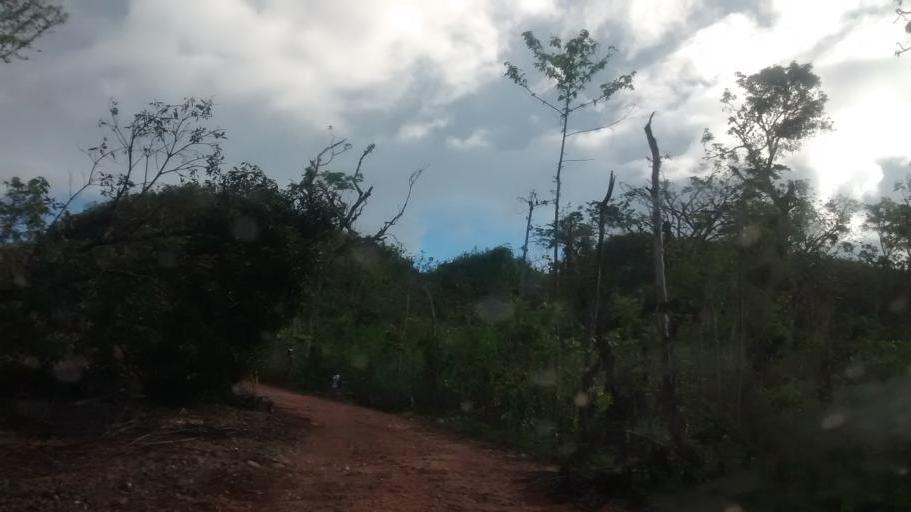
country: HT
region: Grandans
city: Corail
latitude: 18.5097
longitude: -73.7828
